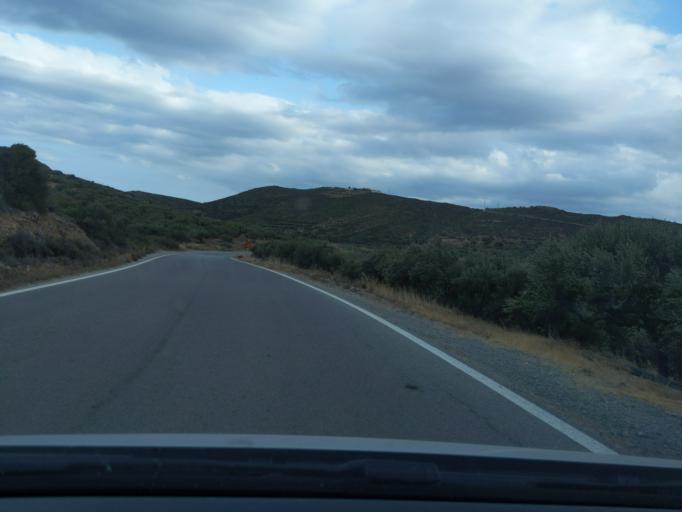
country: GR
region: Crete
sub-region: Nomos Lasithiou
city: Palekastro
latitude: 35.2243
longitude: 26.2573
